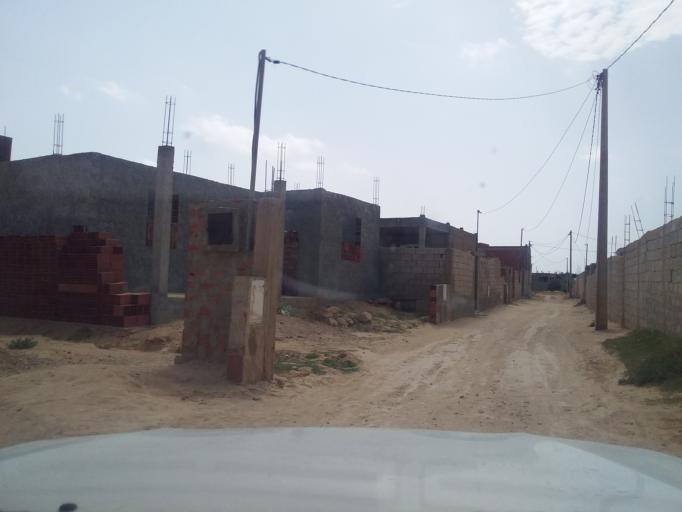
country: TN
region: Qabis
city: Matmata
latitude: 33.6141
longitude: 10.2768
